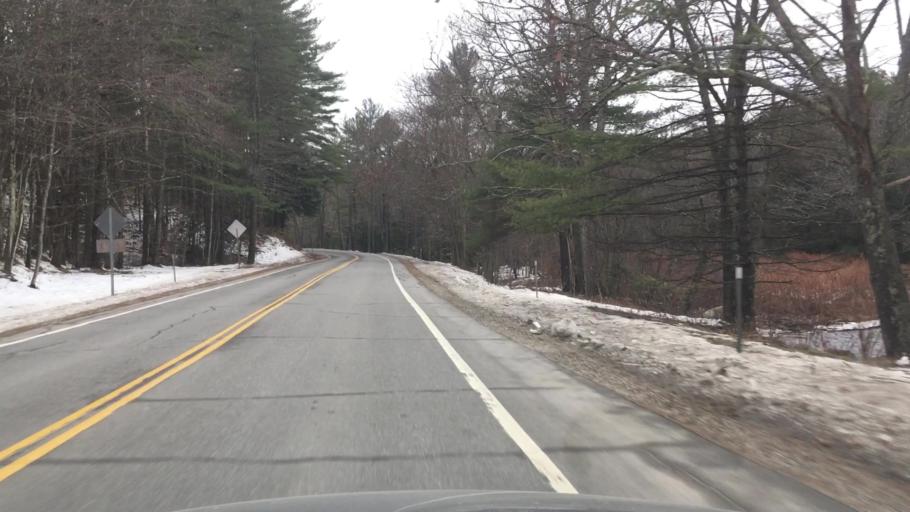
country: US
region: New Hampshire
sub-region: Hillsborough County
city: New Boston
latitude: 43.0012
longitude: -71.6626
